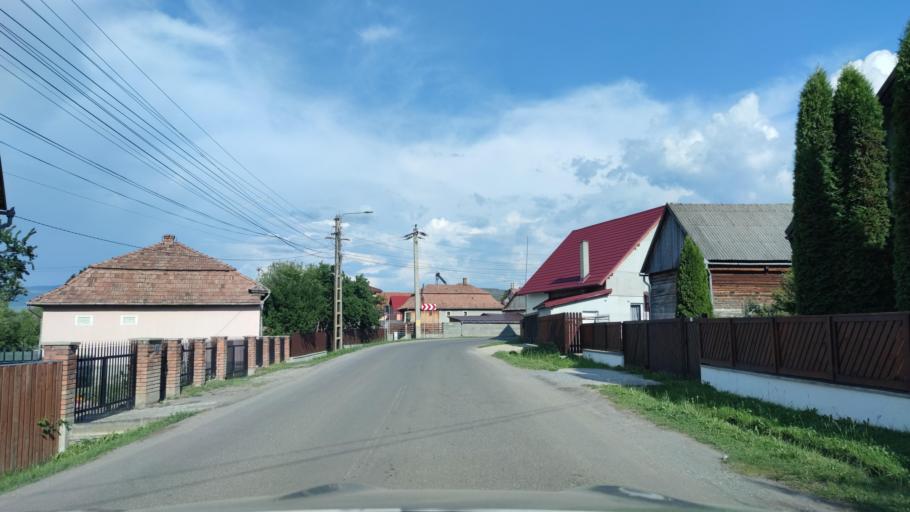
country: RO
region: Harghita
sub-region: Comuna Remetea
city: Remetea
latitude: 46.7936
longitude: 25.4433
